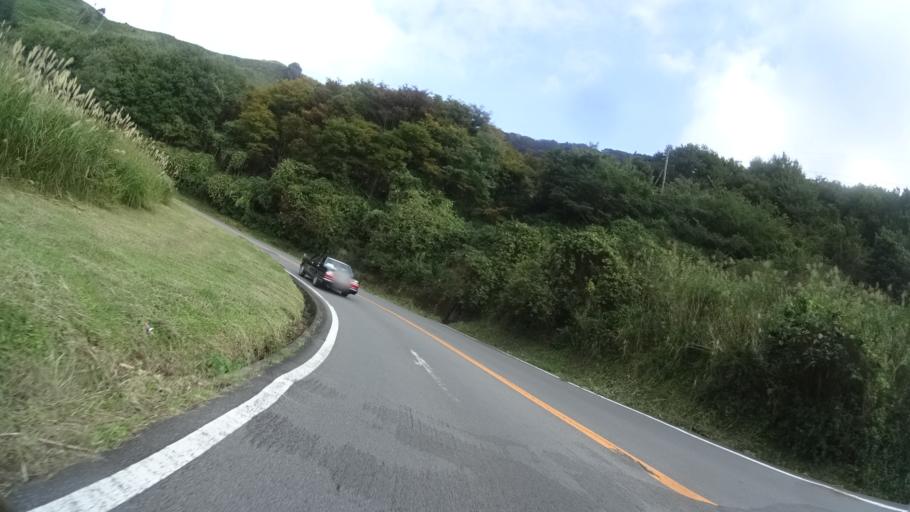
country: JP
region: Oita
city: Beppu
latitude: 33.2578
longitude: 131.3800
